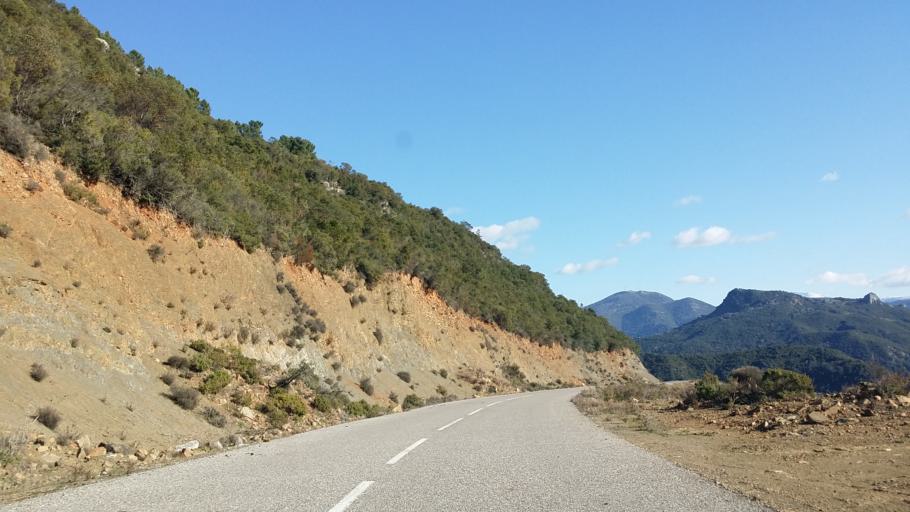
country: GR
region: Central Greece
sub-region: Nomos Evrytanias
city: Kerasochori
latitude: 38.9886
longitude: 21.5012
